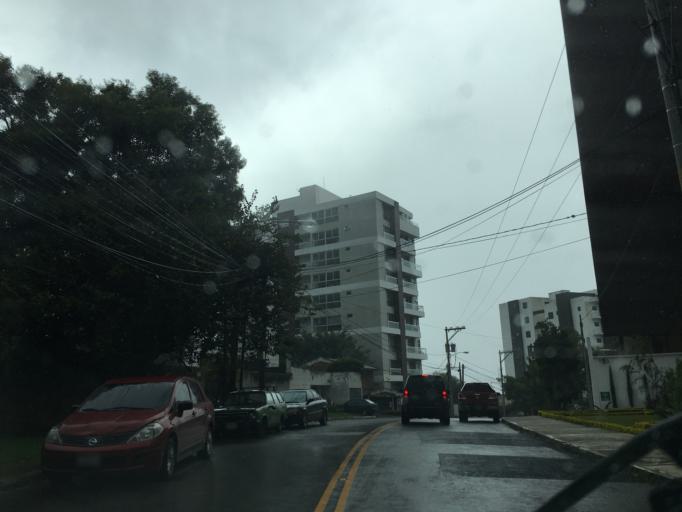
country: GT
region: Guatemala
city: Santa Catarina Pinula
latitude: 14.5812
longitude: -90.4861
